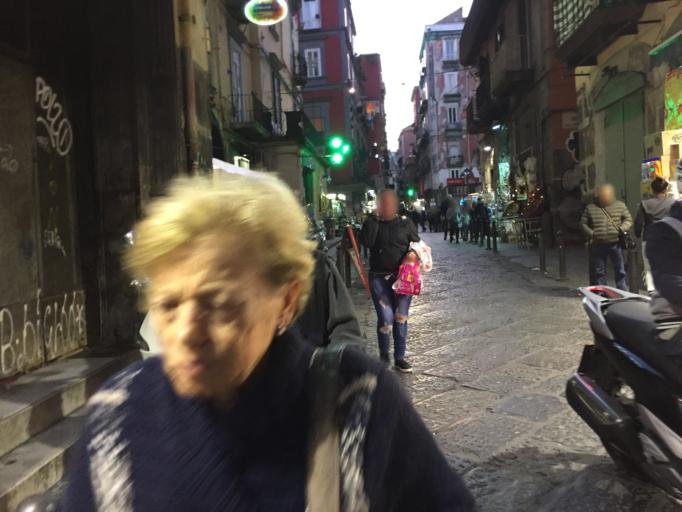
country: IT
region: Campania
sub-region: Provincia di Napoli
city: Napoli
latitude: 40.8514
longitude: 14.2578
